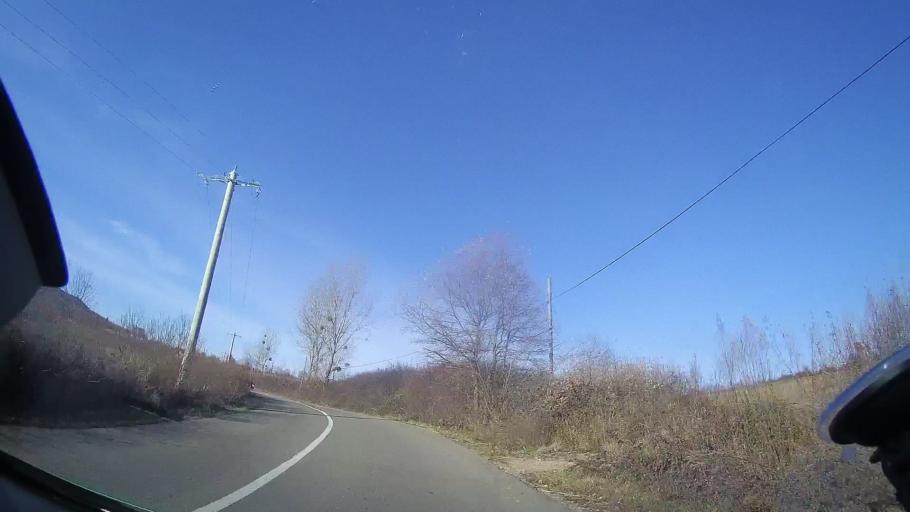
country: RO
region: Bihor
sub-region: Comuna Vadu Crisului
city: Vadu Crisului
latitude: 46.9711
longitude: 22.5469
